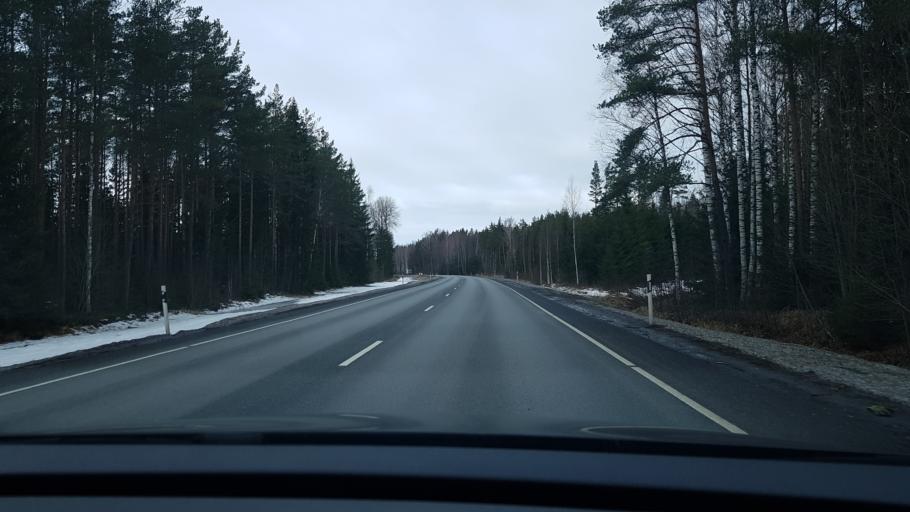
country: EE
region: Paernumaa
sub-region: Paikuse vald
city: Paikuse
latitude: 58.2531
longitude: 24.6828
